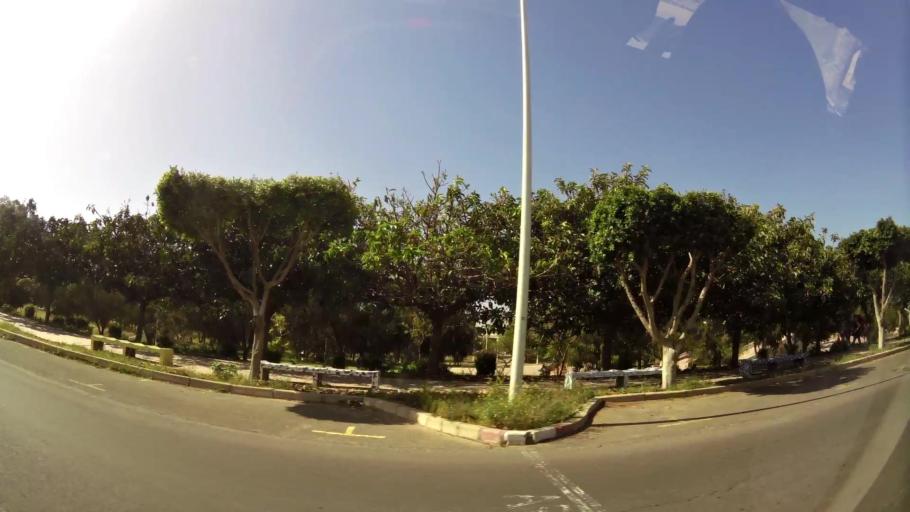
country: MA
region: Souss-Massa-Draa
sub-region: Agadir-Ida-ou-Tnan
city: Agadir
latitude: 30.4195
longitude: -9.5890
